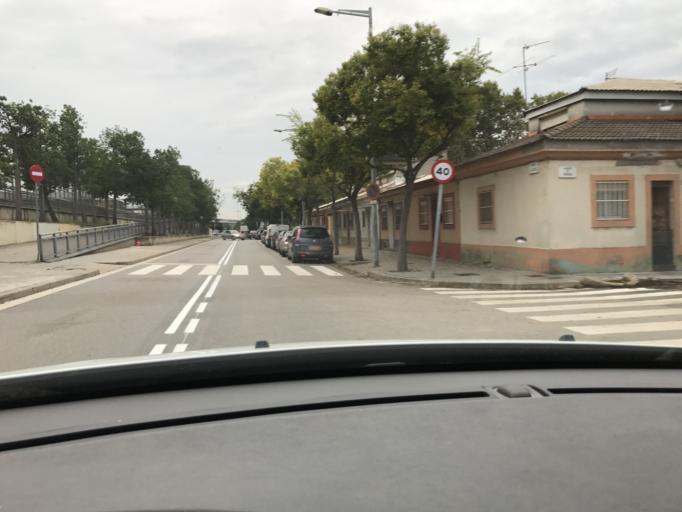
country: ES
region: Catalonia
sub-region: Provincia de Barcelona
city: Llefia
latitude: 41.4381
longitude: 2.2083
